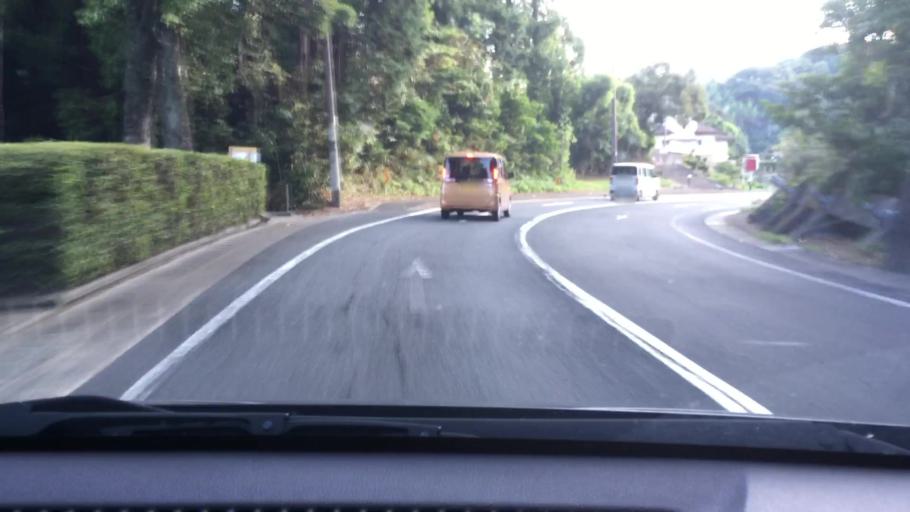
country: JP
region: Nagasaki
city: Togitsu
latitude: 32.9199
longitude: 129.7870
